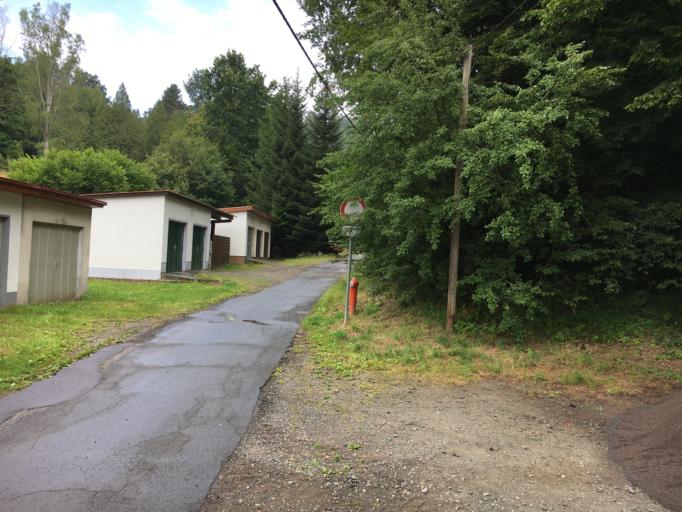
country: DE
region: Thuringia
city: Schmalkalden
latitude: 50.7221
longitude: 10.4264
